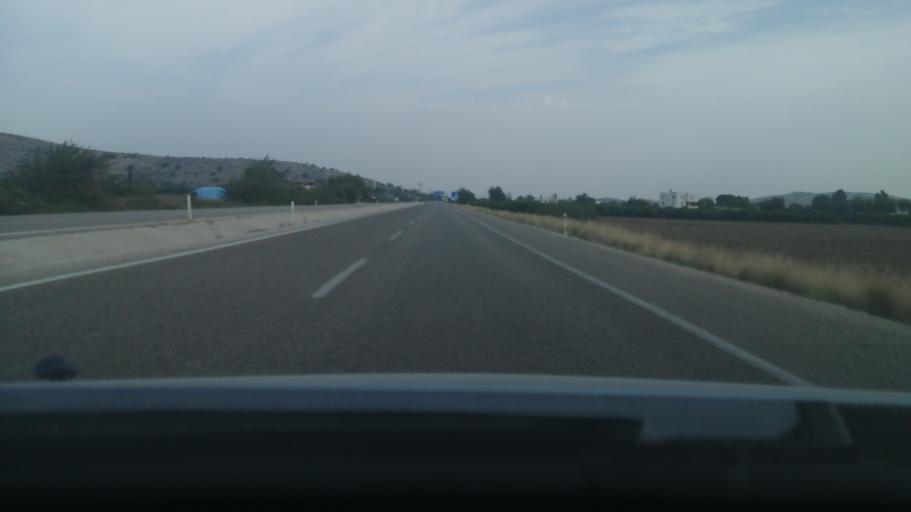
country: TR
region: Adana
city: Kozan
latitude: 37.3826
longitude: 35.8172
